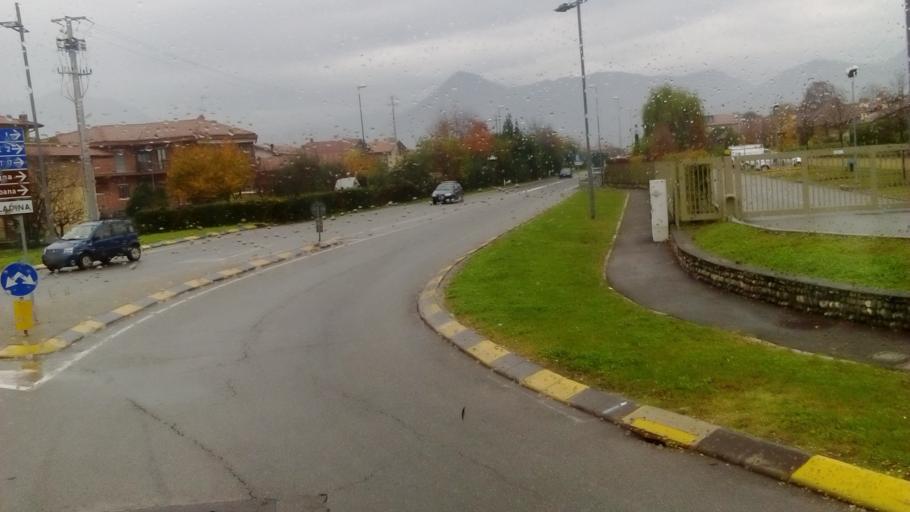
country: IT
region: Lombardy
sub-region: Provincia di Bergamo
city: Paladina
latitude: 45.7270
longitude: 9.6092
